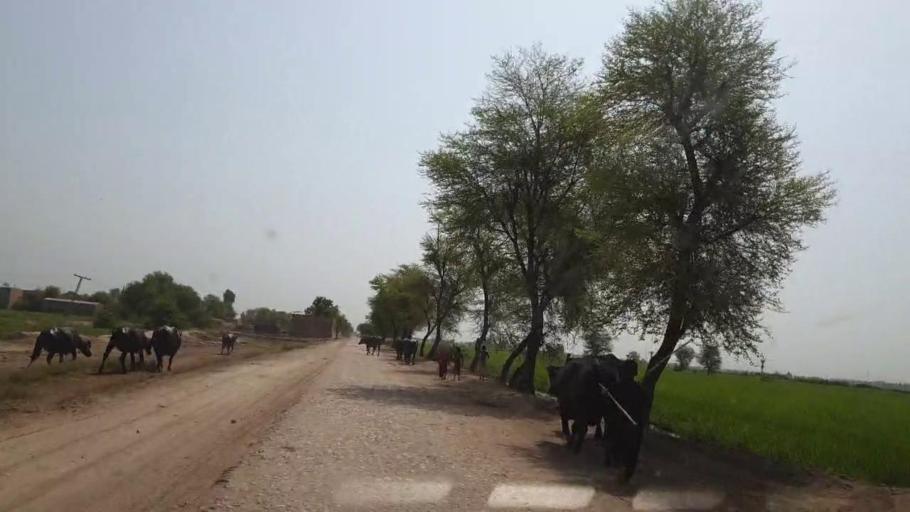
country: PK
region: Sindh
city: Lakhi
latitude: 27.8787
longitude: 68.6621
